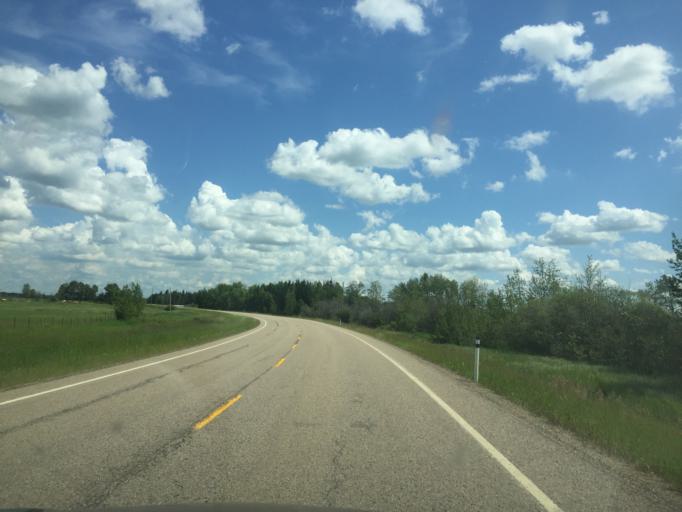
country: CA
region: Alberta
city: Athabasca
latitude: 54.3271
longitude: -113.3198
